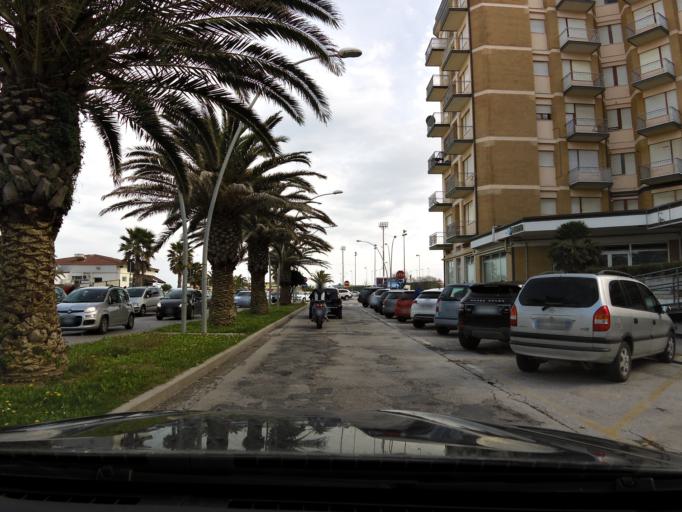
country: IT
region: The Marches
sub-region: Provincia di Macerata
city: Portocivitanova
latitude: 43.3009
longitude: 13.7380
